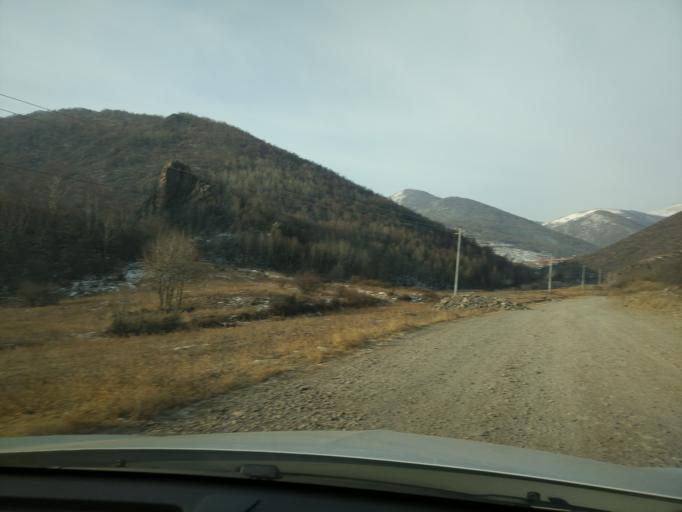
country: CN
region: Hebei
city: Xiwanzi
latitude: 40.8514
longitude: 115.4787
